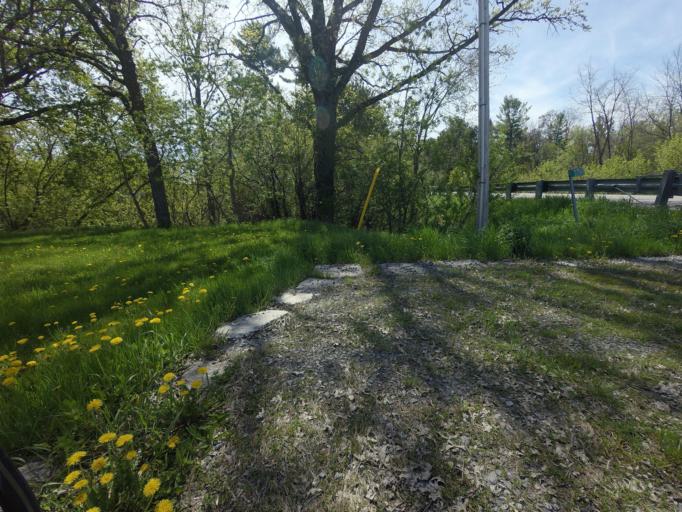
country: CA
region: Ontario
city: Arnprior
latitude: 45.4076
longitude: -76.1620
